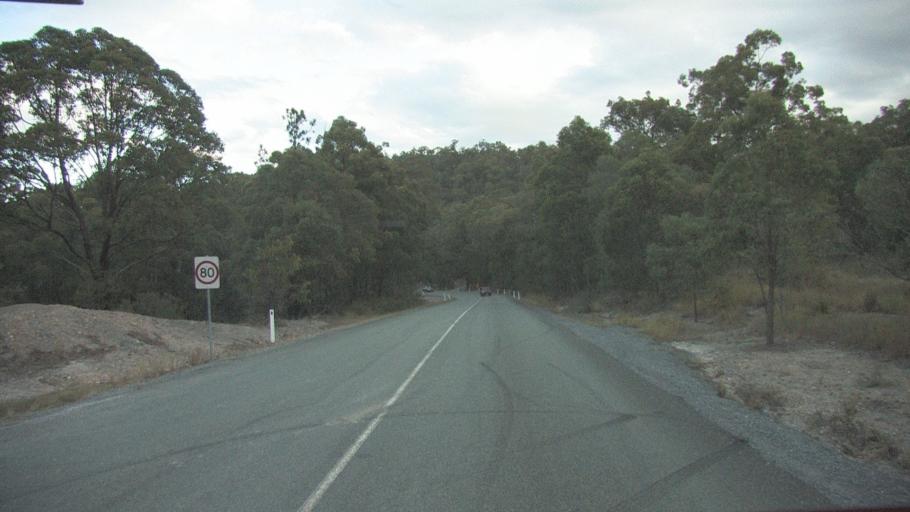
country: AU
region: Queensland
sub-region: Logan
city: Chambers Flat
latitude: -27.8022
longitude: 153.1441
